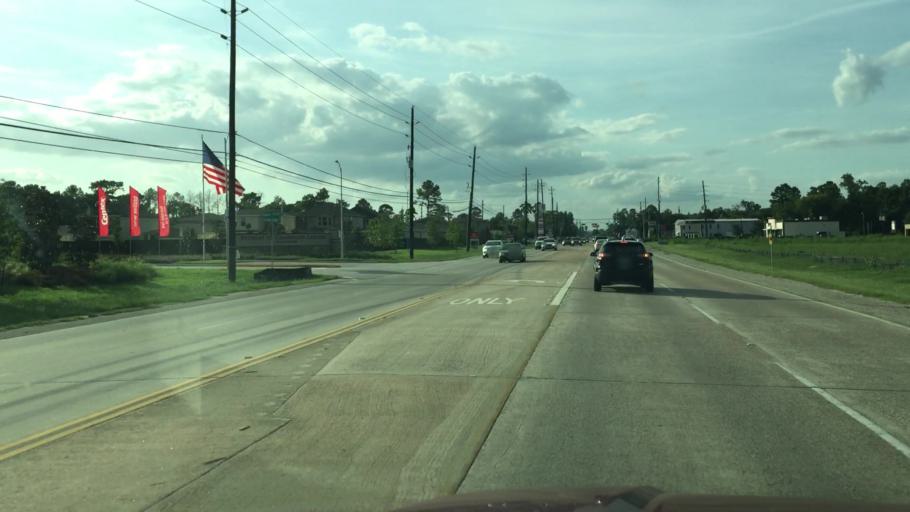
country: US
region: Texas
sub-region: Harris County
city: Hudson
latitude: 29.9969
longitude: -95.5050
